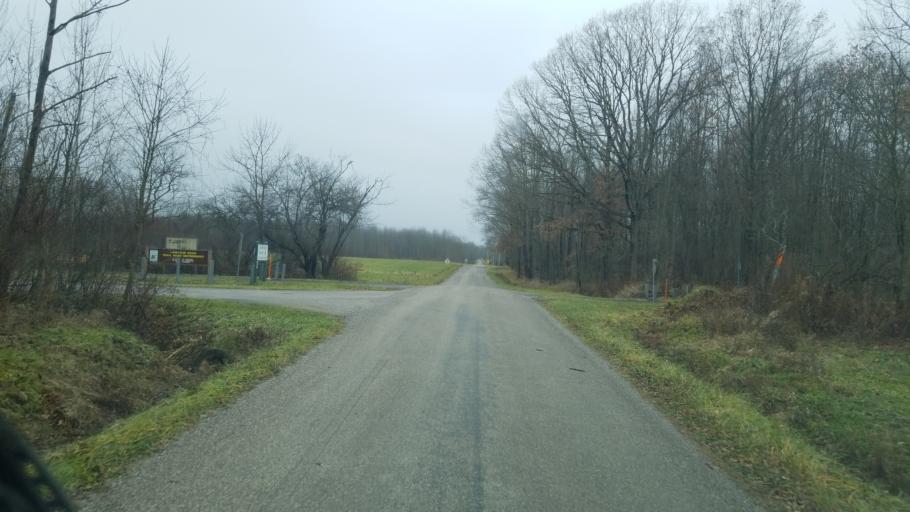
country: US
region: Ohio
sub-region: Ashtabula County
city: Jefferson
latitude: 41.7530
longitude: -80.8435
